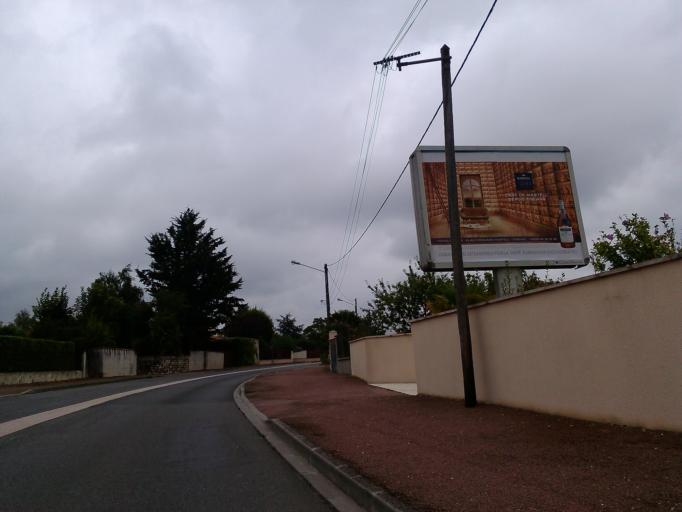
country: FR
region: Poitou-Charentes
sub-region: Departement de la Charente
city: Cognac
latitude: 45.6950
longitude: -0.3472
